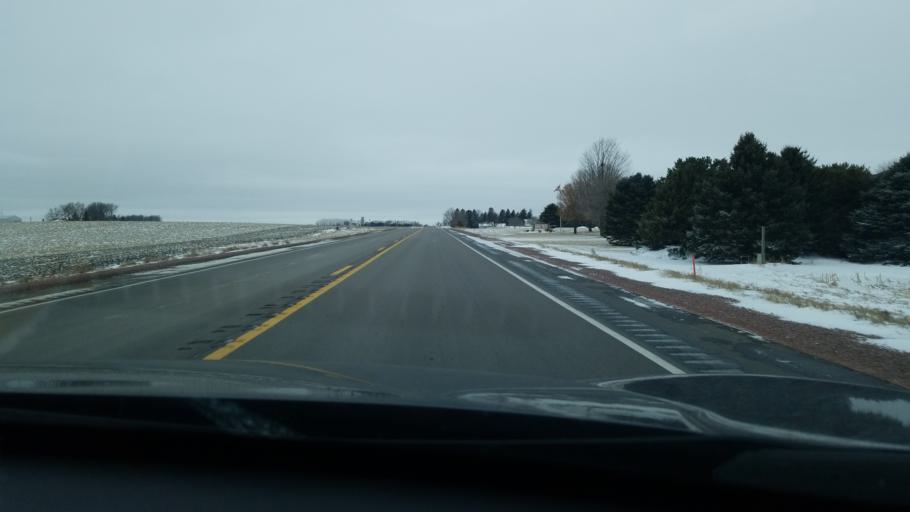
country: US
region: Iowa
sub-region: Lyon County
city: Rock Rapids
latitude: 43.4330
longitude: -96.3721
